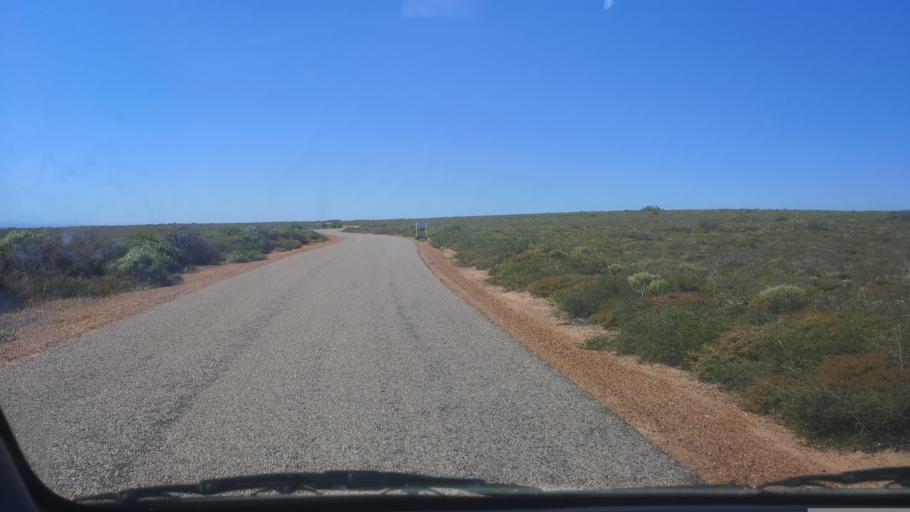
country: AU
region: Western Australia
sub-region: Northampton Shire
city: Kalbarri
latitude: -27.8224
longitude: 114.1161
